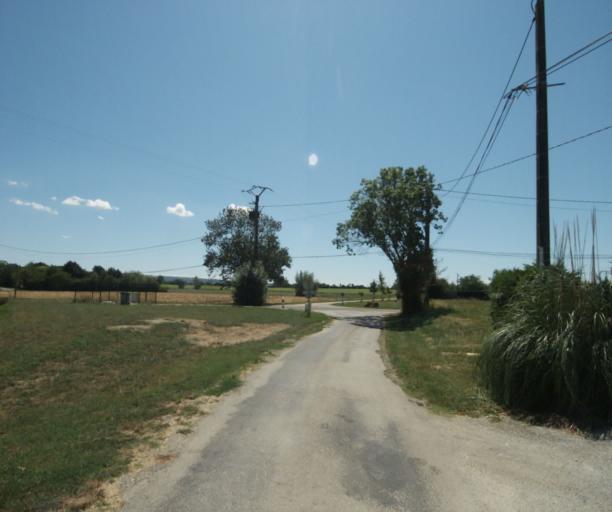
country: FR
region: Midi-Pyrenees
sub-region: Departement de la Haute-Garonne
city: Saint-Felix-Lauragais
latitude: 43.4638
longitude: 1.9330
